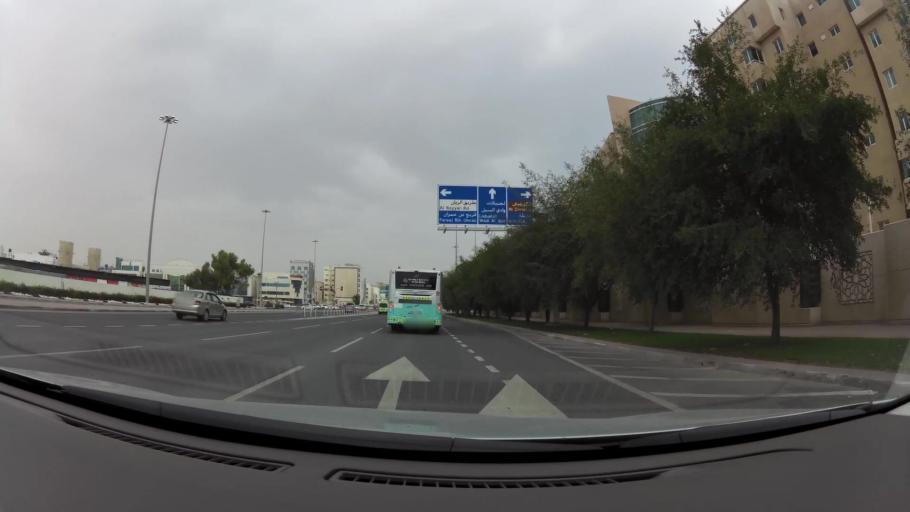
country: QA
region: Baladiyat ad Dawhah
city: Doha
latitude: 25.2990
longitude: 51.5032
